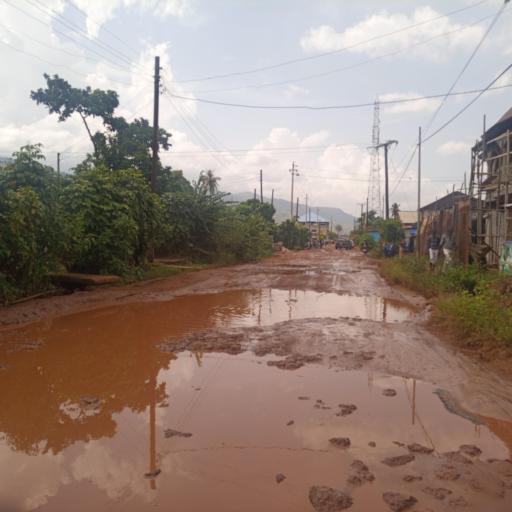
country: SL
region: Western Area
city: Hastings
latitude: 8.3856
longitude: -13.1454
